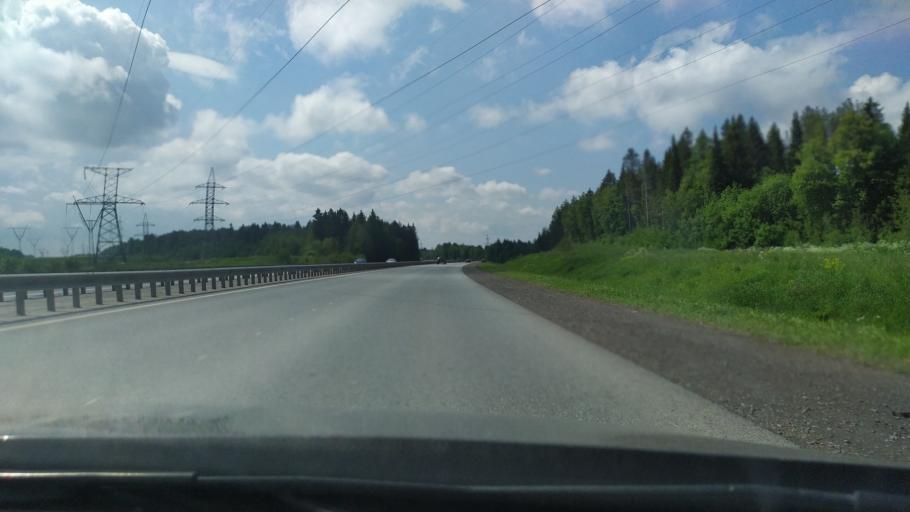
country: RU
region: Perm
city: Ferma
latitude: 58.0164
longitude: 56.4112
